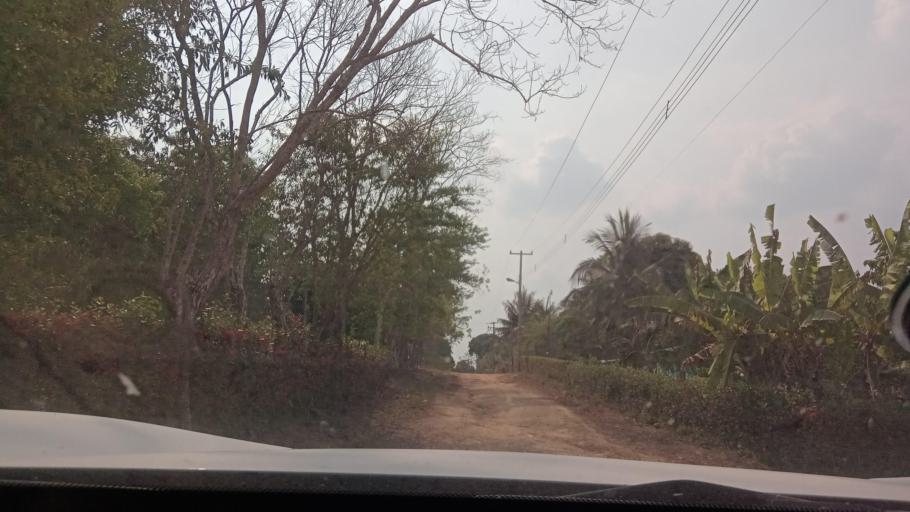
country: MX
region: Tabasco
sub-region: Huimanguillo
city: Francisco Rueda
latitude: 17.6911
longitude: -93.8327
